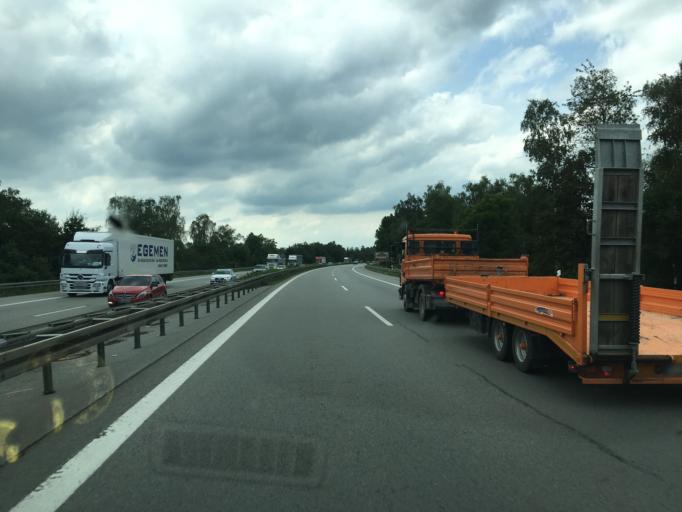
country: DE
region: Bavaria
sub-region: Lower Bavaria
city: Aicha vorm Wald
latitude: 48.6455
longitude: 13.2873
